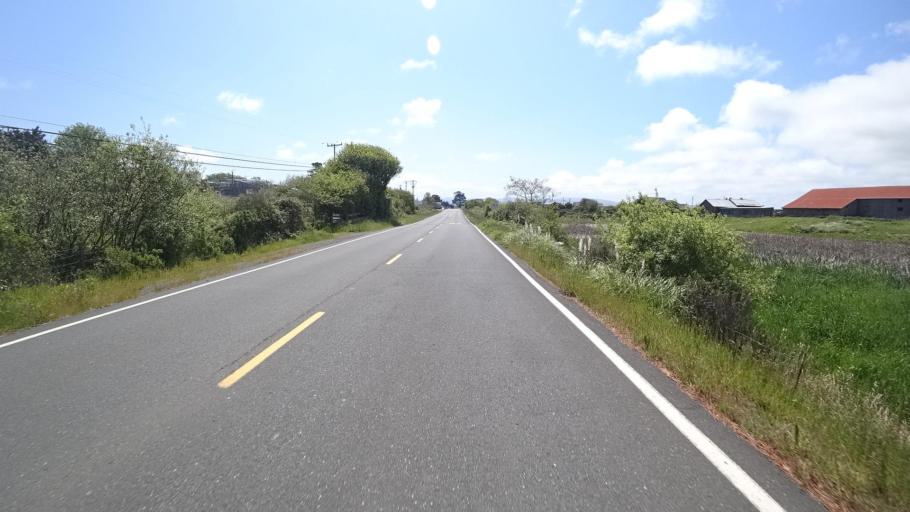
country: US
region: California
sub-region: Humboldt County
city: Ferndale
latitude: 40.6448
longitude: -124.2264
